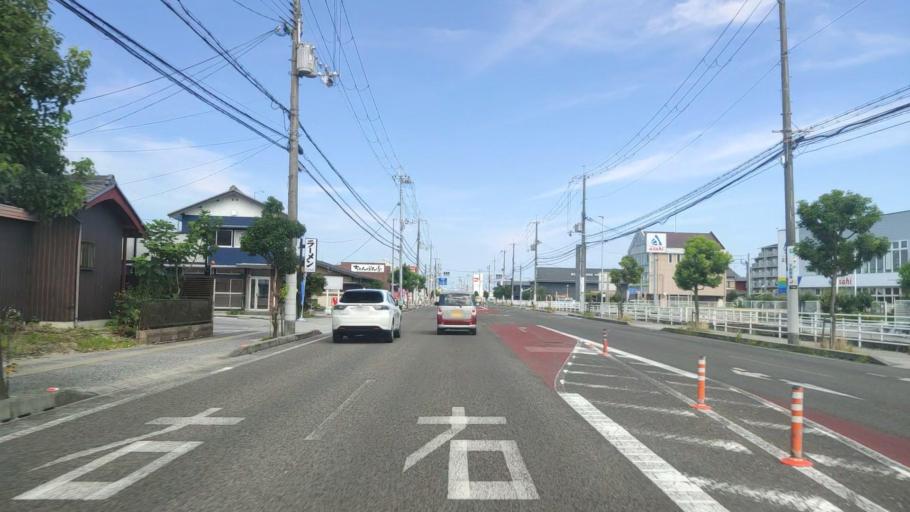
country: JP
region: Shiga Prefecture
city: Hikone
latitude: 35.2544
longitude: 136.2394
